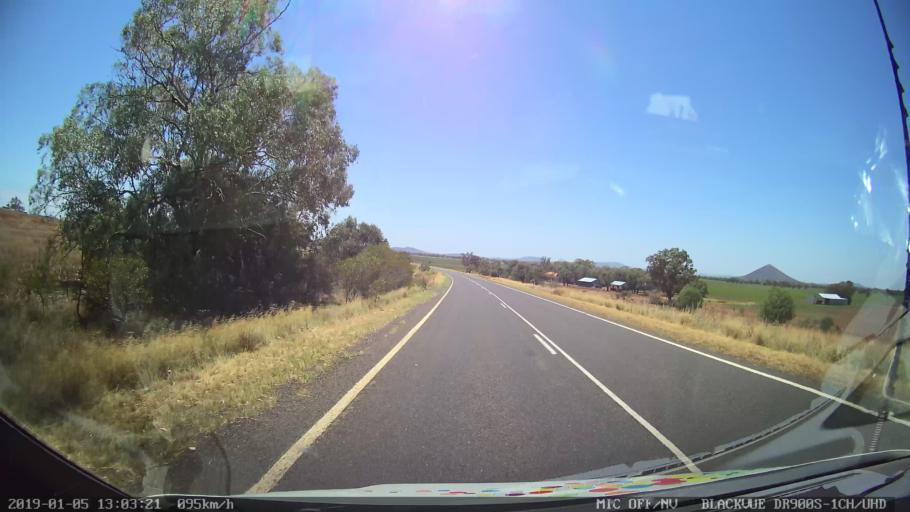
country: AU
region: New South Wales
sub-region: Gunnedah
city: Gunnedah
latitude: -31.1116
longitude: 149.8261
